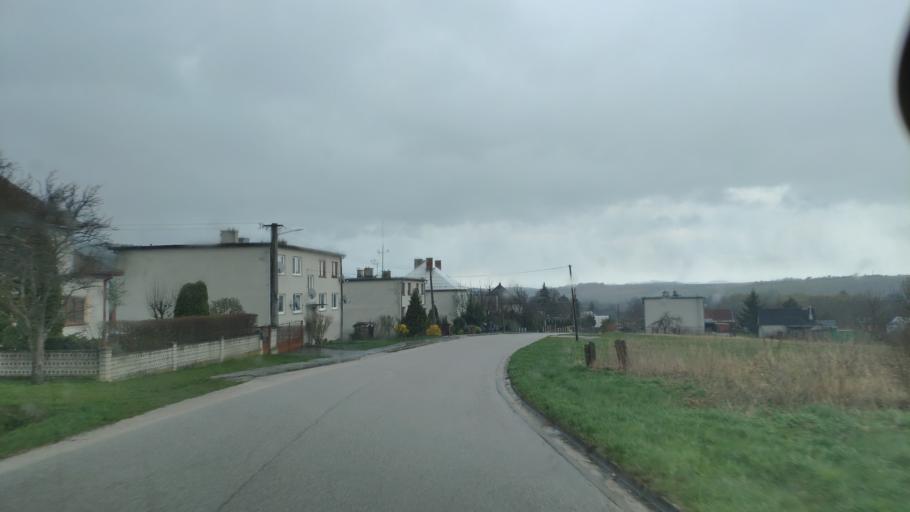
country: SK
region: Nitriansky
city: Stara Tura
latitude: 48.8089
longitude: 17.7102
